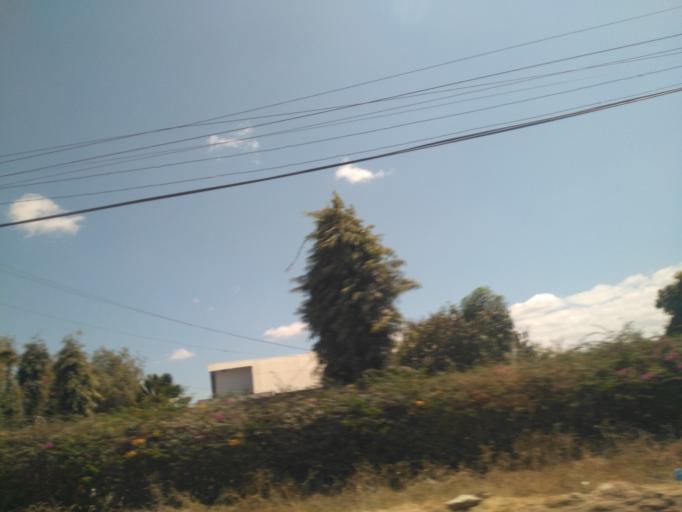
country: TZ
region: Dodoma
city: Kisasa
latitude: -6.1651
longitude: 35.7674
